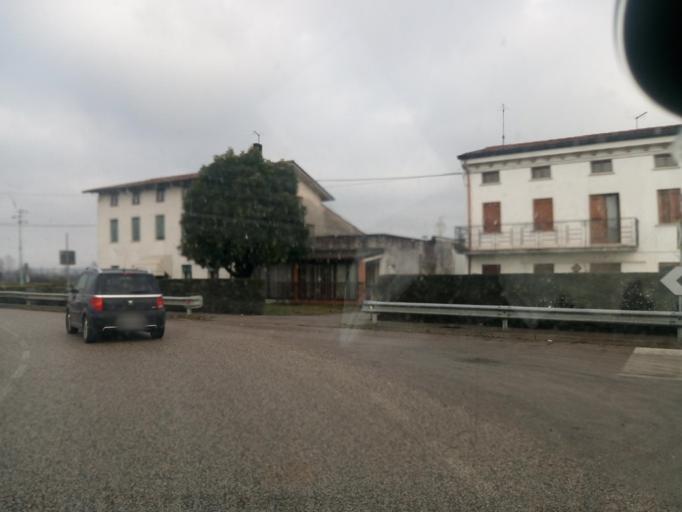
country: IT
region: Veneto
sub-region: Provincia di Vicenza
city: Bressanvido
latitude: 45.6632
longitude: 11.6427
